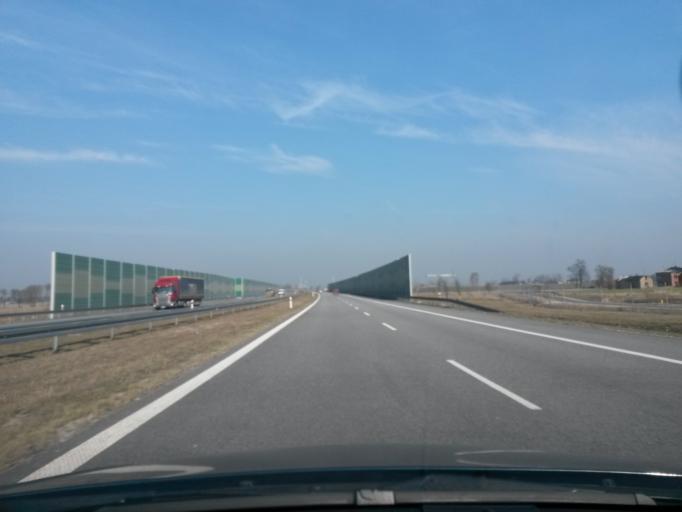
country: PL
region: Lodz Voivodeship
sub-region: Powiat kutnowski
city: Krzyzanow
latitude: 52.2004
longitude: 19.4858
